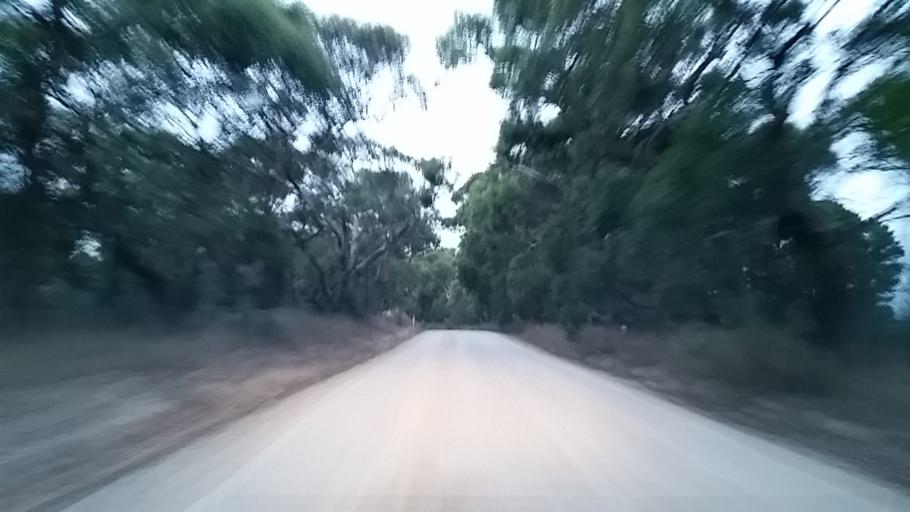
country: AU
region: South Australia
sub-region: Yankalilla
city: Normanville
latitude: -35.6107
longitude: 138.1700
